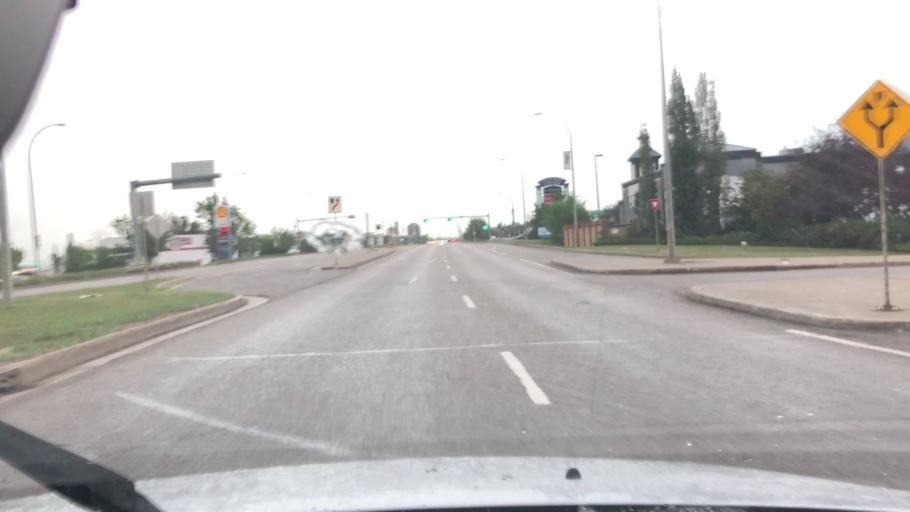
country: CA
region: Alberta
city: St. Albert
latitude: 53.5434
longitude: -113.6150
